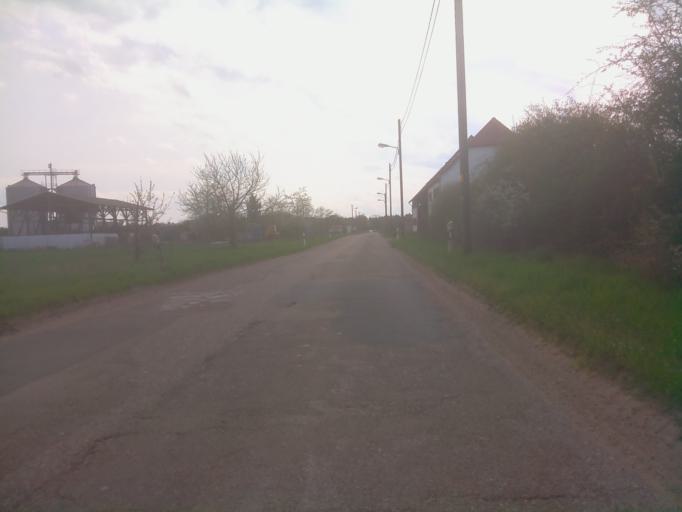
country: DE
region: Hesse
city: Lampertheim
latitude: 49.5721
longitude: 8.4948
